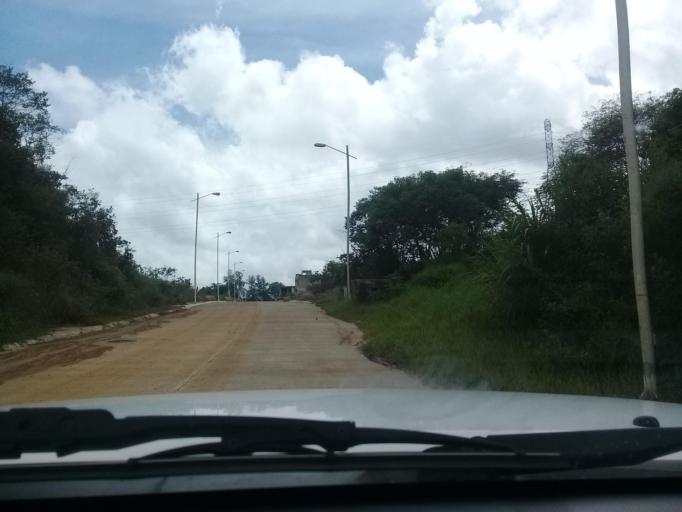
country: MX
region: Veracruz
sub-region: Xalapa
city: Lomas Verdes
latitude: 19.5005
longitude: -96.9128
